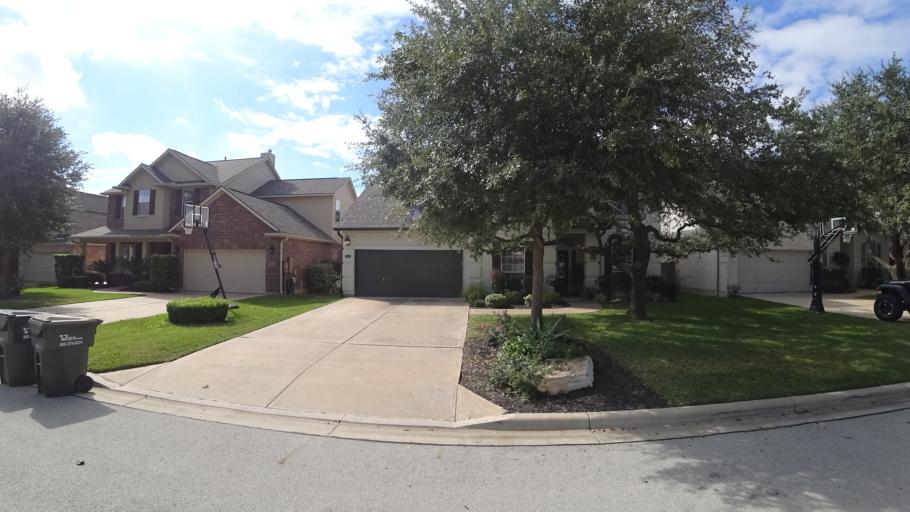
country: US
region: Texas
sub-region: Travis County
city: Hudson Bend
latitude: 30.3673
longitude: -97.9067
